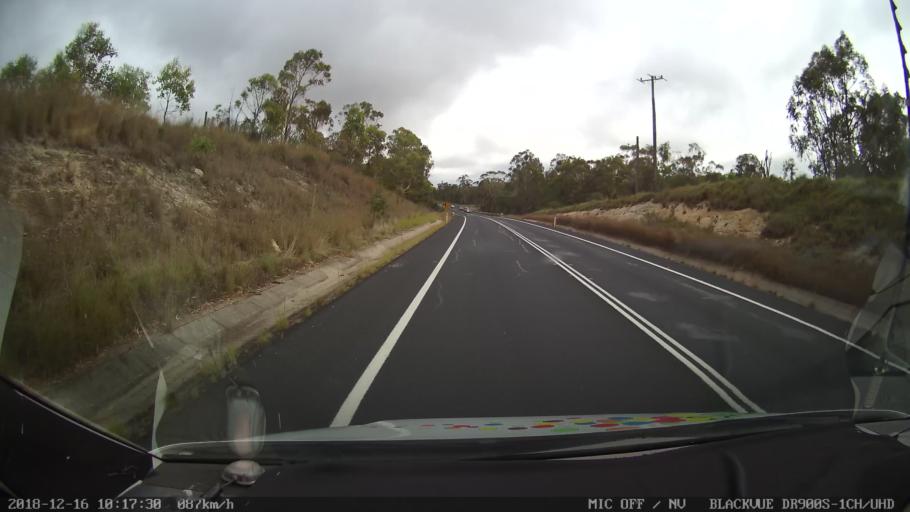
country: AU
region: New South Wales
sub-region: Tenterfield Municipality
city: Carrolls Creek
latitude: -29.2553
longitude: 151.9923
